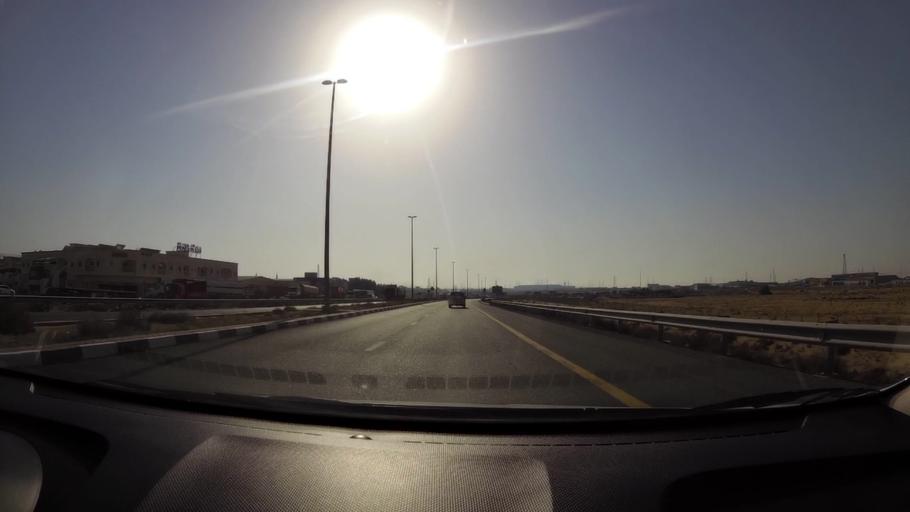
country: AE
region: Ajman
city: Ajman
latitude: 25.4408
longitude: 55.5524
